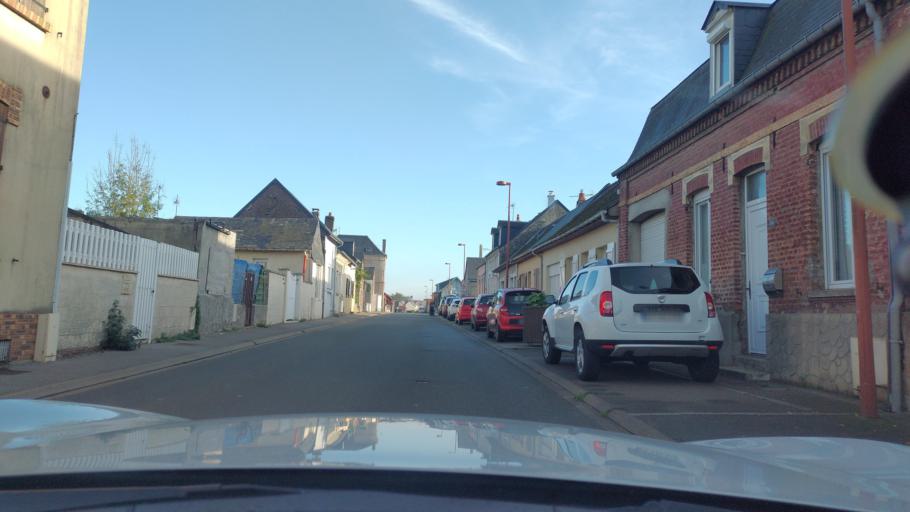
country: FR
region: Picardie
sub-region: Departement de la Somme
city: Fressenneville
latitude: 50.0670
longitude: 1.5793
